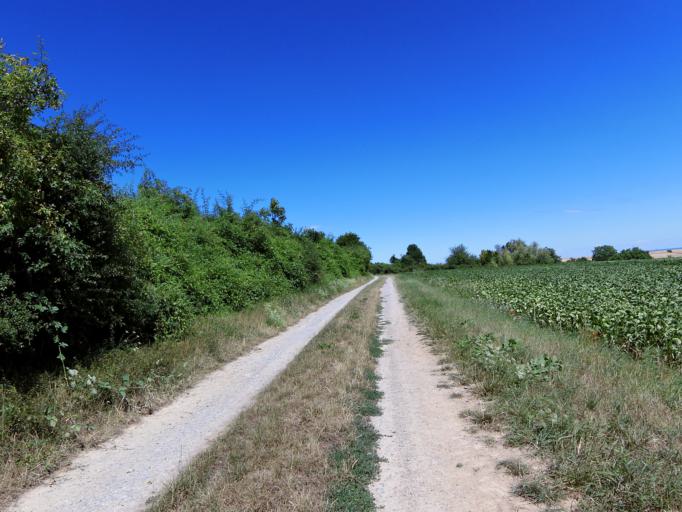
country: DE
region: Bavaria
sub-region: Regierungsbezirk Unterfranken
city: Gerbrunn
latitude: 49.7657
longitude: 10.0058
